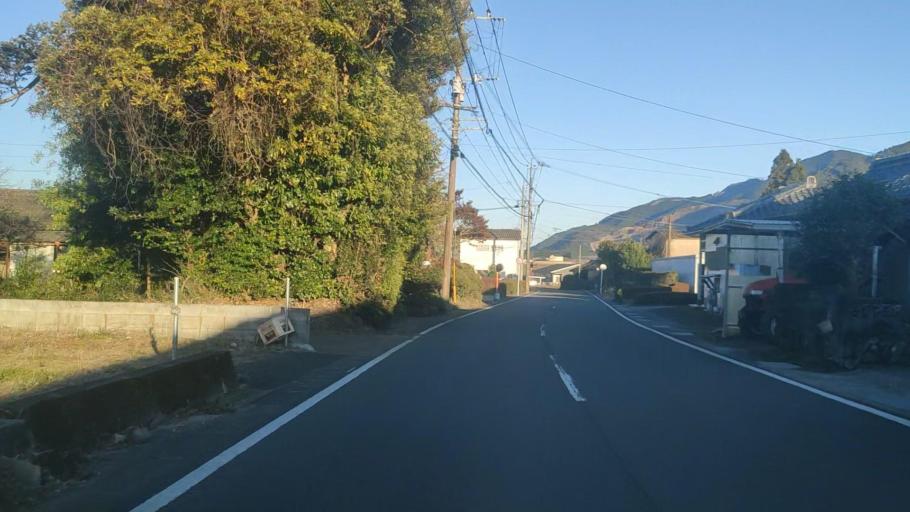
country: JP
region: Miyazaki
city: Miyazaki-shi
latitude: 31.8260
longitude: 131.3012
